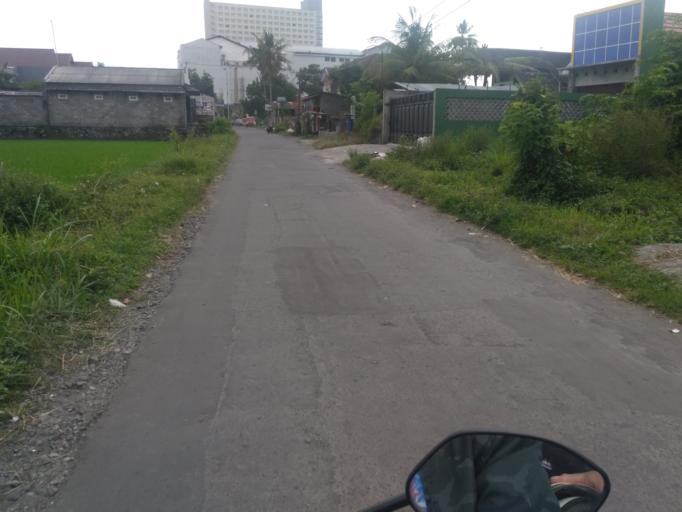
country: ID
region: Daerah Istimewa Yogyakarta
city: Melati
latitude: -7.7568
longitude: 110.3596
